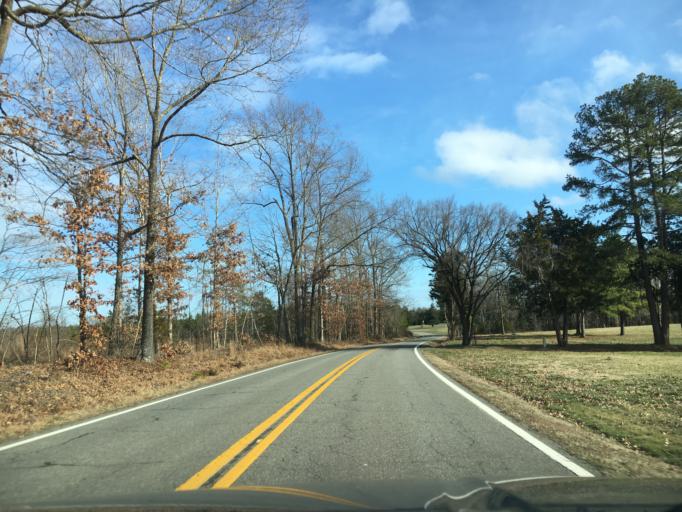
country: US
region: Virginia
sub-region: Halifax County
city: South Boston
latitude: 36.7338
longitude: -78.8723
